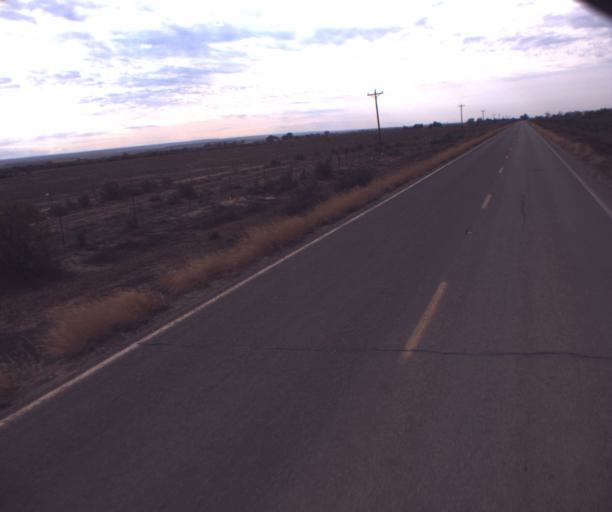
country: US
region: Arizona
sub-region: Apache County
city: Many Farms
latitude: 36.4328
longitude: -109.6069
